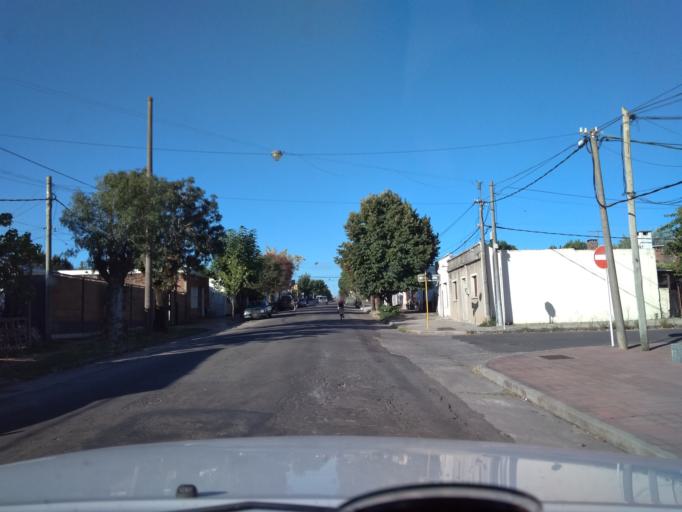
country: UY
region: Florida
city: Florida
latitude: -34.0962
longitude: -56.2236
